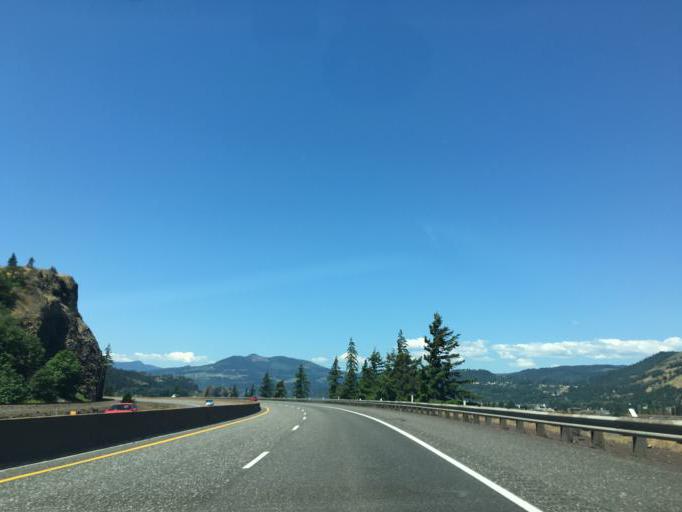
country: US
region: Washington
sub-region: Klickitat County
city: White Salmon
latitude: 45.6949
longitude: -121.4457
